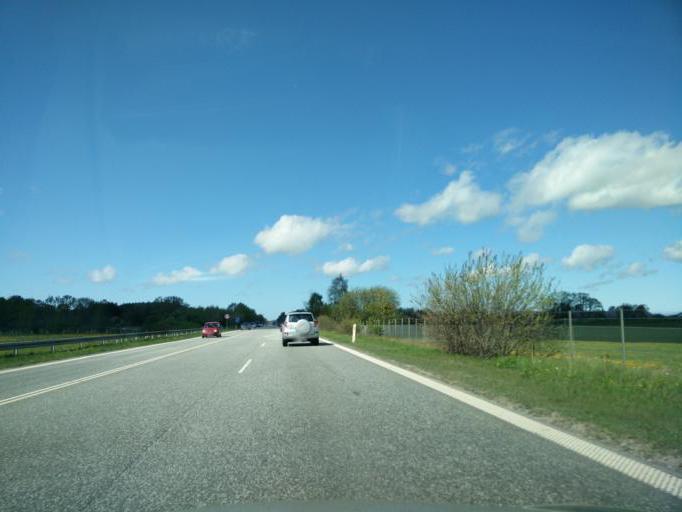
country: DK
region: Capital Region
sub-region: Hillerod Kommune
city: Hillerod
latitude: 55.9203
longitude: 12.2603
